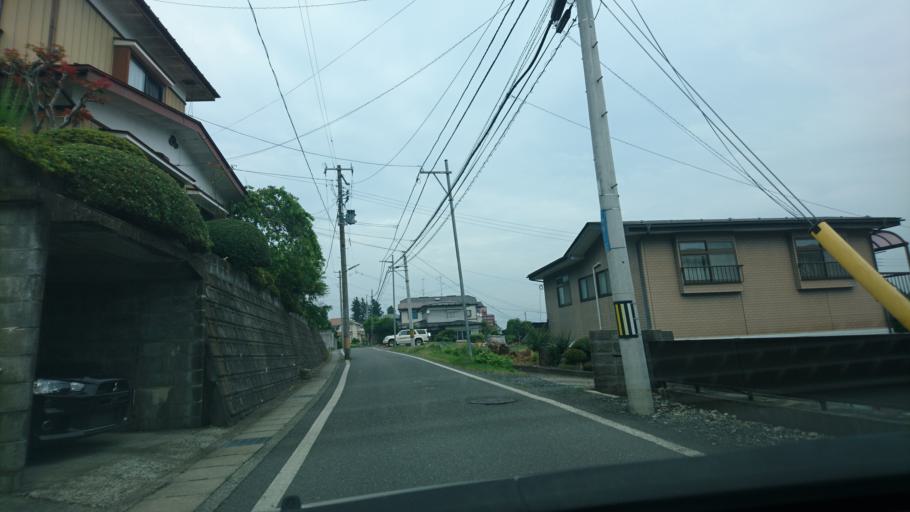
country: JP
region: Iwate
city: Ichinoseki
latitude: 38.9166
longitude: 141.1286
